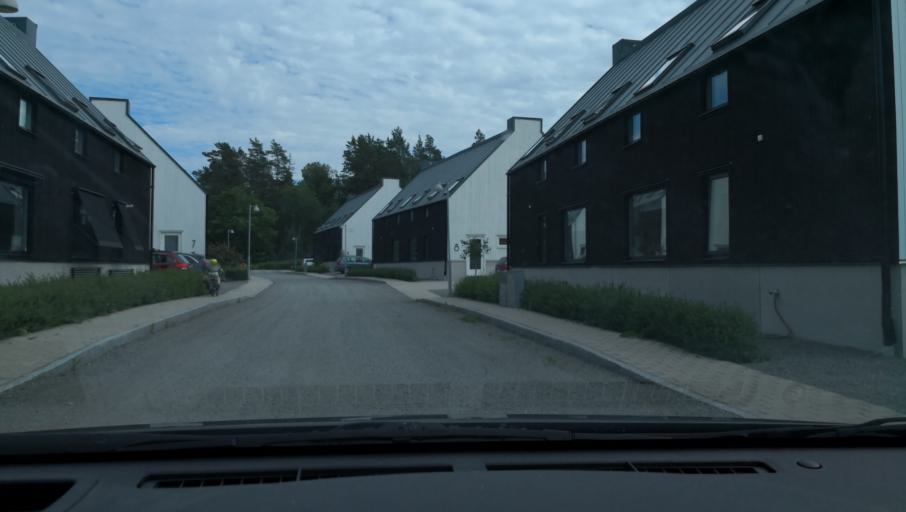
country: SE
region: Uppsala
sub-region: Uppsala Kommun
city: Uppsala
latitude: 59.8078
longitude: 17.5331
